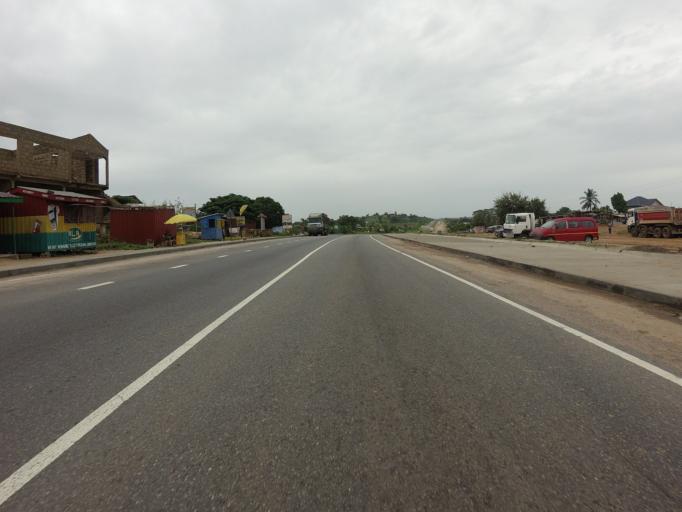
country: GH
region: Eastern
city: Nsawam
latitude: 5.9013
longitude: -0.3895
